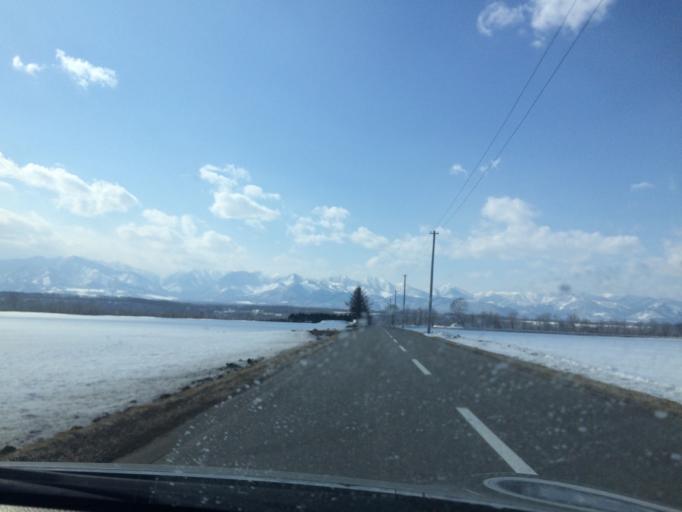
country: JP
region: Hokkaido
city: Otofuke
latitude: 42.9608
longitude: 142.9780
